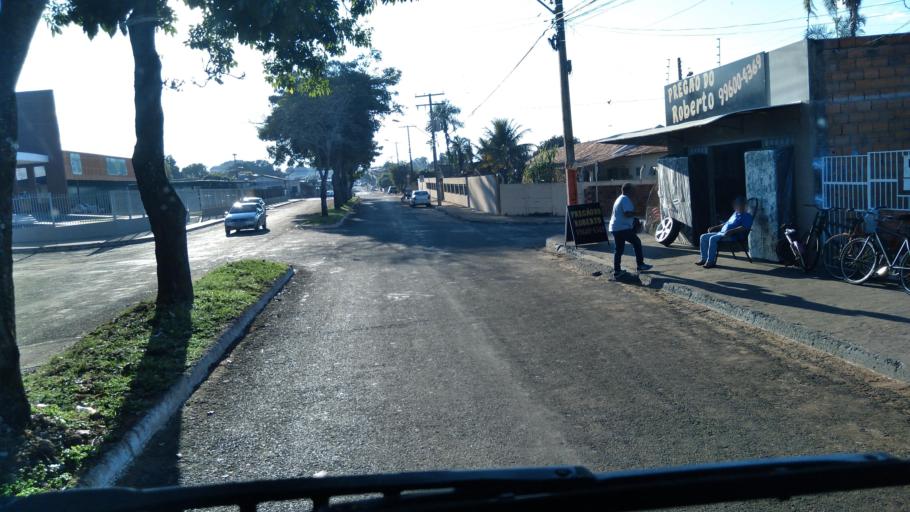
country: BR
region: Goias
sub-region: Mineiros
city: Mineiros
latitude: -17.5743
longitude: -52.5643
